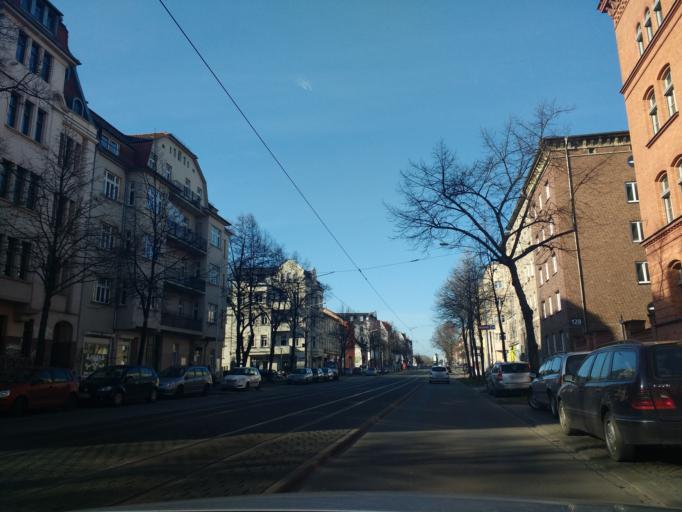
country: DE
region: Saxony-Anhalt
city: Halle (Saale)
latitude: 51.4983
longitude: 11.9665
